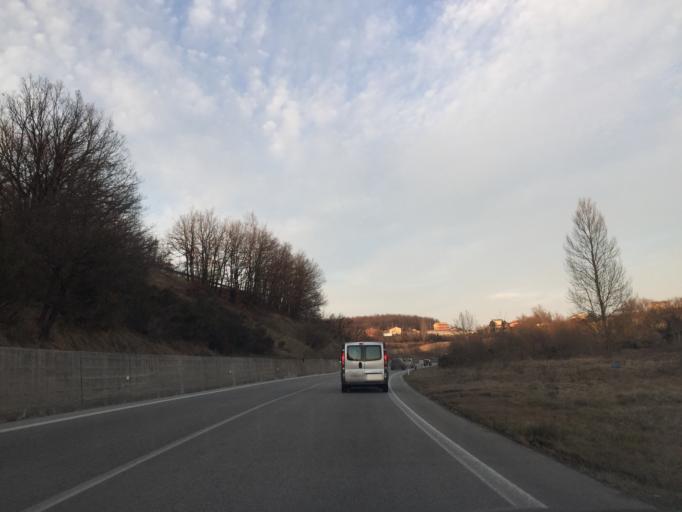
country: IT
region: Molise
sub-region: Provincia di Campobasso
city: Mimosa-Poggio Verde-Nuova Comunita
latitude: 41.5436
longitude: 14.6231
